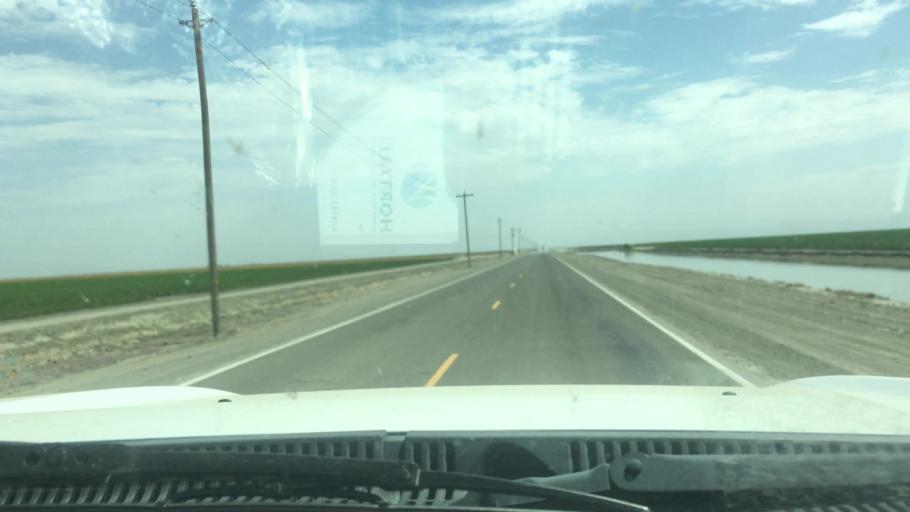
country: US
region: California
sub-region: Tulare County
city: Alpaugh
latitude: 35.9094
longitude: -119.5734
